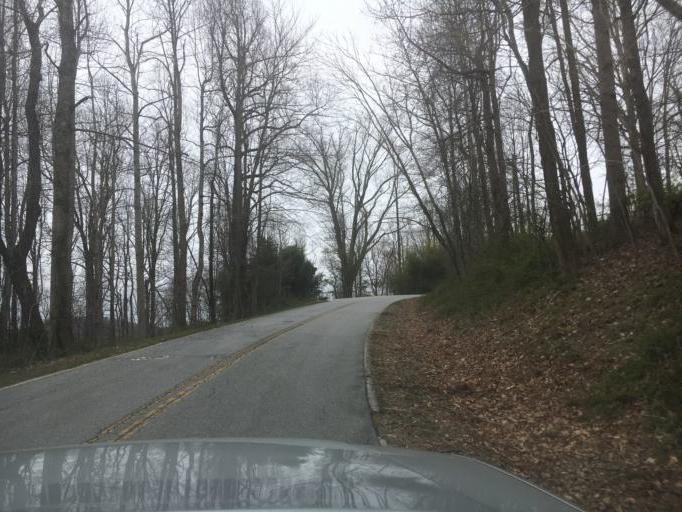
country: US
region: North Carolina
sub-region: Henderson County
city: East Flat Rock
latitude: 35.2457
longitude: -82.4136
